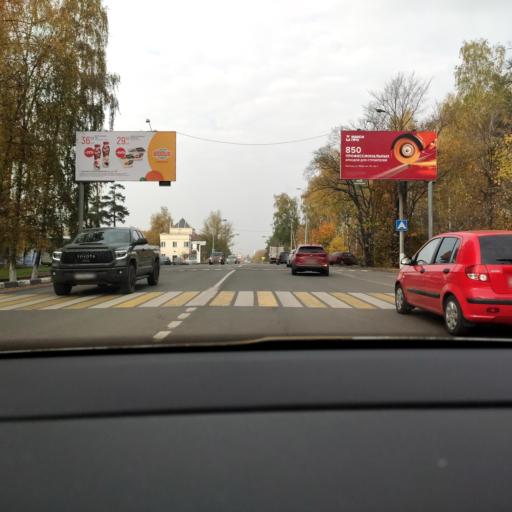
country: RU
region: Moskovskaya
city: Lesnyye Polyany
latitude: 55.9831
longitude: 37.8859
